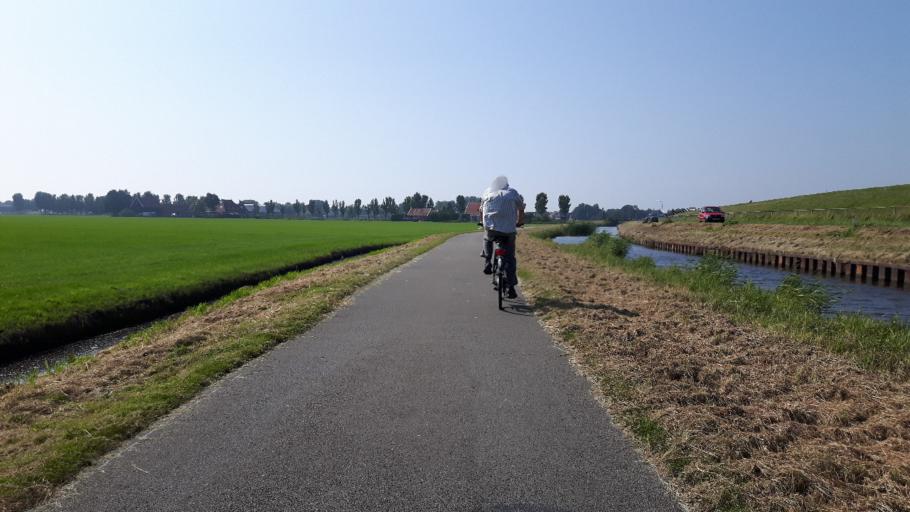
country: NL
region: Friesland
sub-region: Sudwest Fryslan
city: Koudum
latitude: 52.9424
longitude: 5.4133
